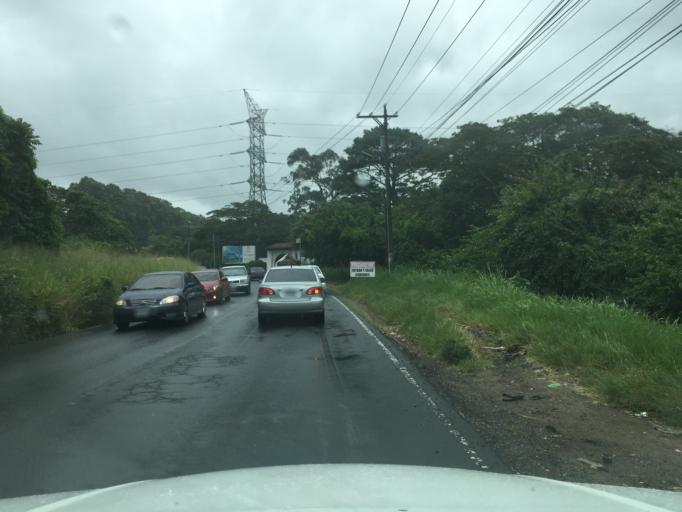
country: GT
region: Guatemala
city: Petapa
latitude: 14.5341
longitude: -90.5290
